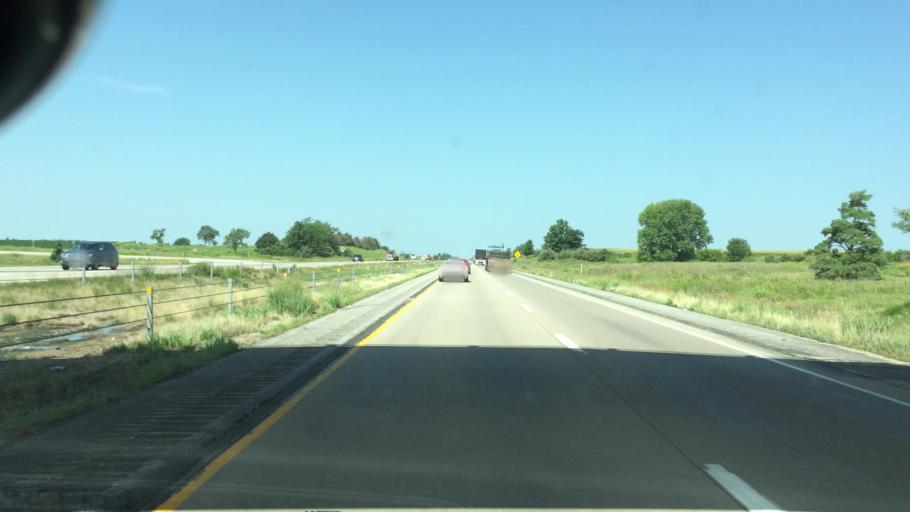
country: US
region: Iowa
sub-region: Iowa County
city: Williamsburg
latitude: 41.6889
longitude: -92.0663
